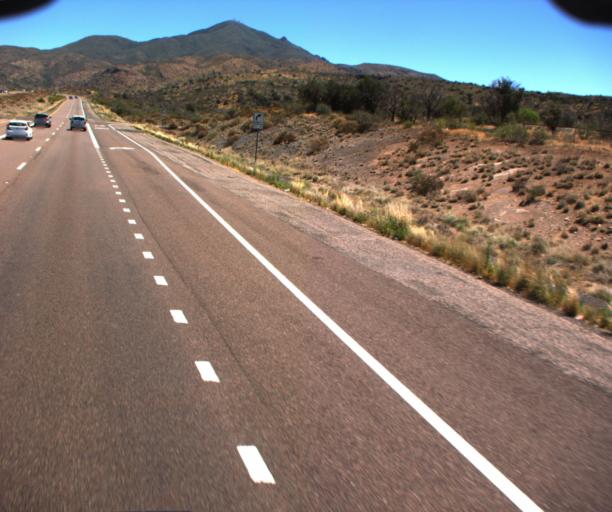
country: US
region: Arizona
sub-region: Gila County
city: Tonto Basin
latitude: 33.8693
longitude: -111.4657
